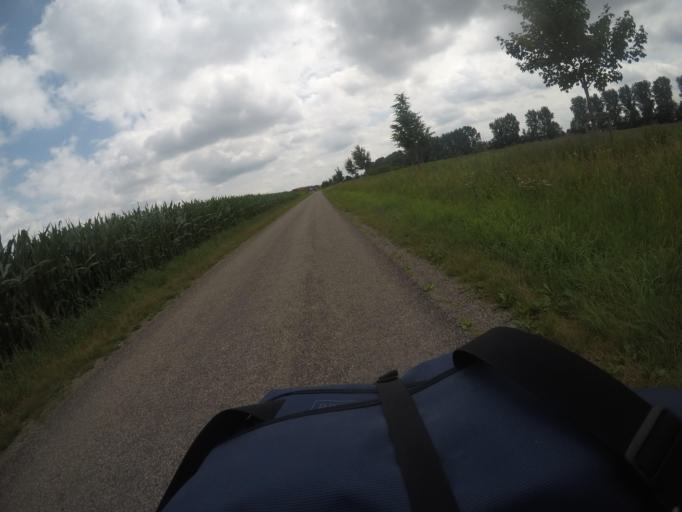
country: DE
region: Bavaria
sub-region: Swabia
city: Heimertingen
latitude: 48.0218
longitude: 10.1707
